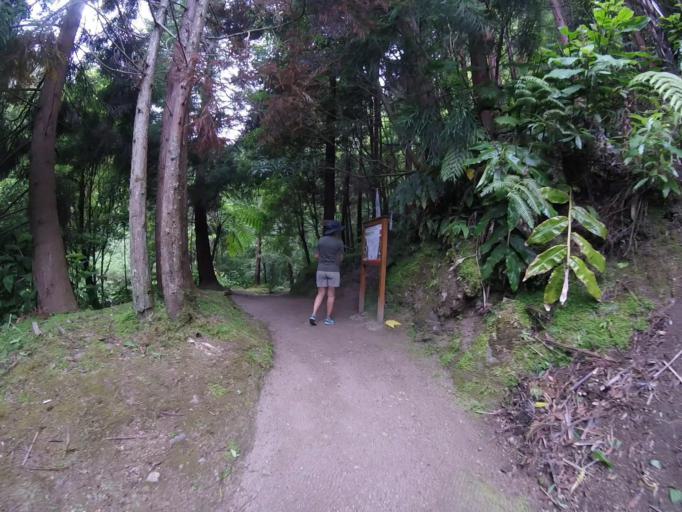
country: PT
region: Azores
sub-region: Vila Franca do Campo
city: Vila Franca do Campo
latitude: 37.7469
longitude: -25.5127
